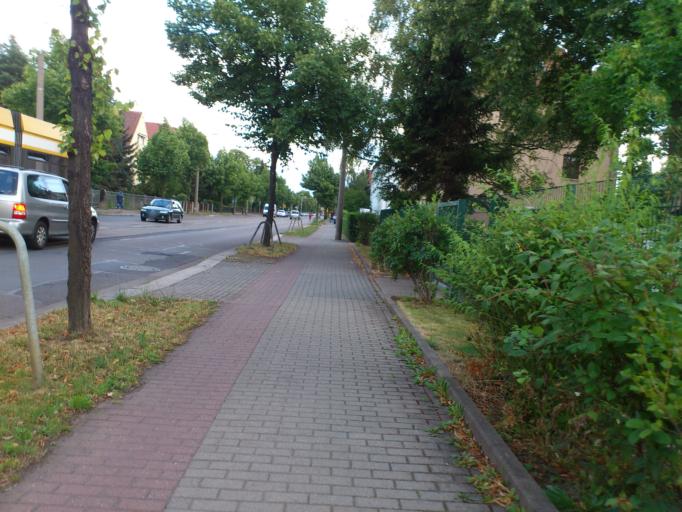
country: DE
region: Saxony
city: Dresden
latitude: 51.0237
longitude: 13.7724
